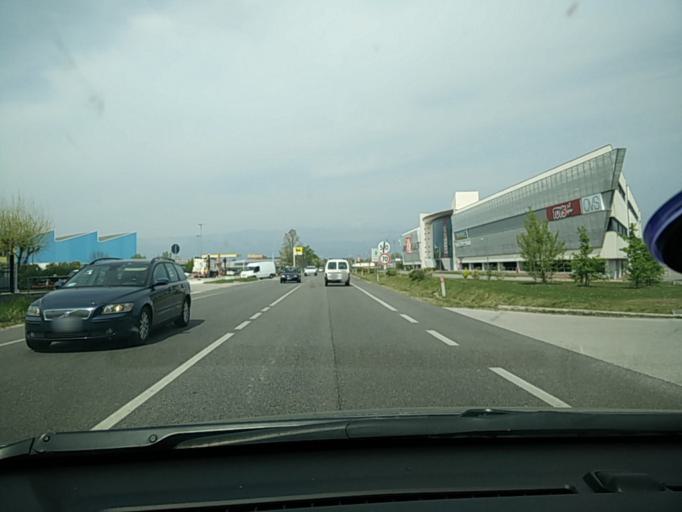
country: IT
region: Friuli Venezia Giulia
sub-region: Provincia di Pordenone
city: Pordenone
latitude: 45.9511
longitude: 12.6890
